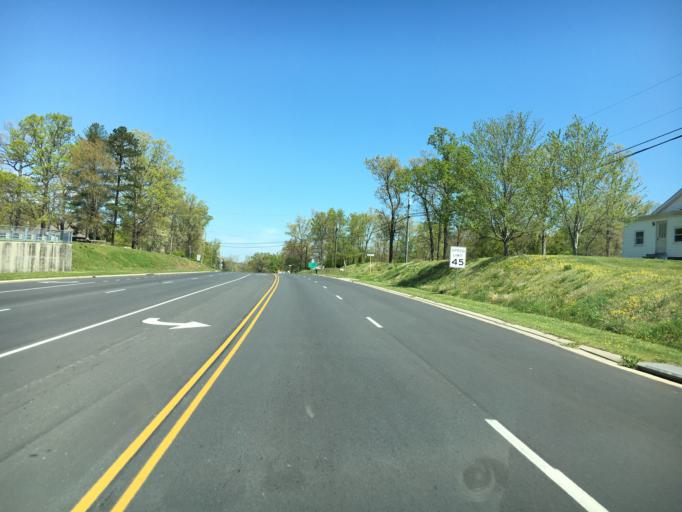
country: US
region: Virginia
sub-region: Augusta County
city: Crimora
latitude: 38.1543
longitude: -78.8427
